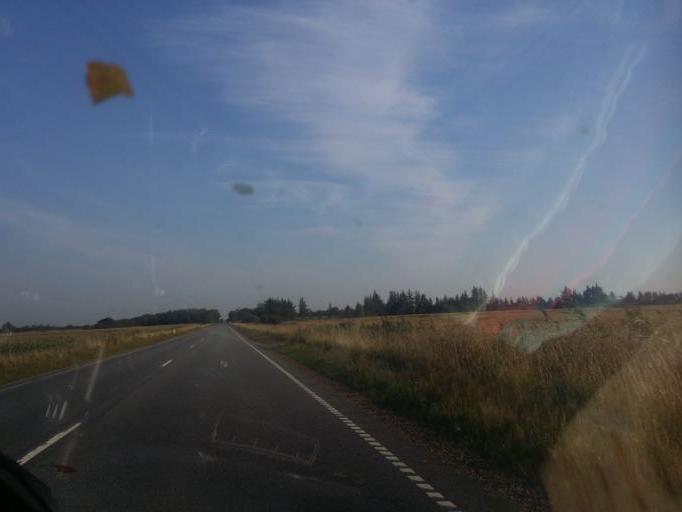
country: DK
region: South Denmark
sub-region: Tonder Kommune
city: Sherrebek
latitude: 55.0923
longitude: 8.8196
